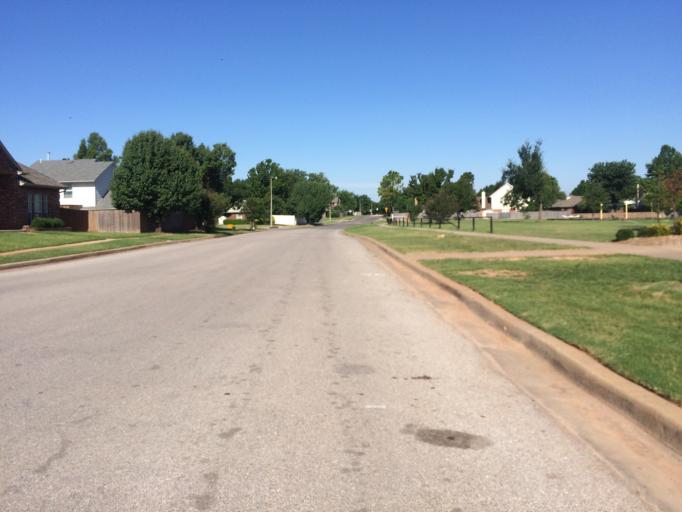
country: US
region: Oklahoma
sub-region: Cleveland County
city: Norman
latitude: 35.2390
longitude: -97.4366
